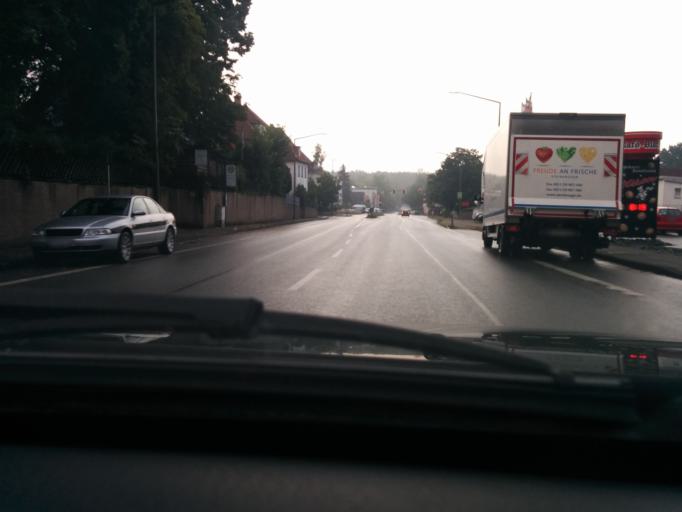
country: DE
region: North Rhine-Westphalia
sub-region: Regierungsbezirk Detmold
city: Bielefeld
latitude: 52.0003
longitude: 8.4914
